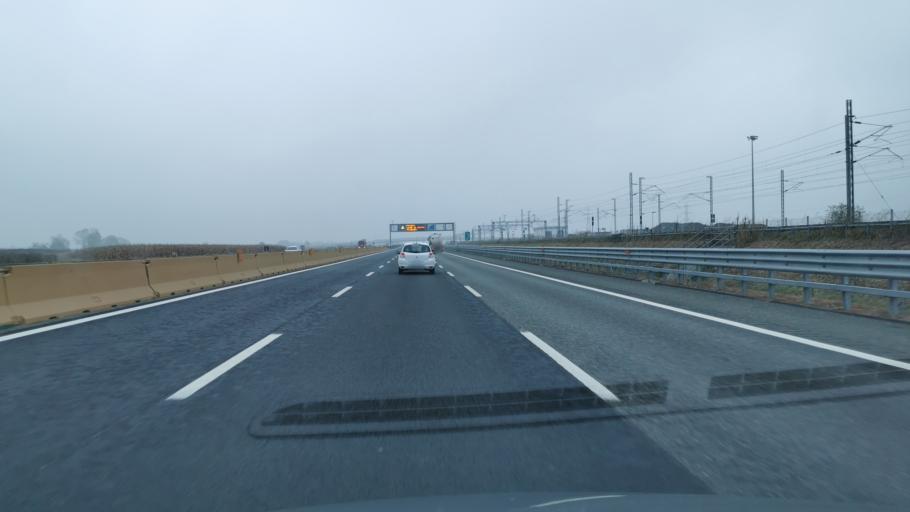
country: IT
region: Piedmont
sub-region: Provincia di Vercelli
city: Alice Castello
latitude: 45.3466
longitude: 8.1008
